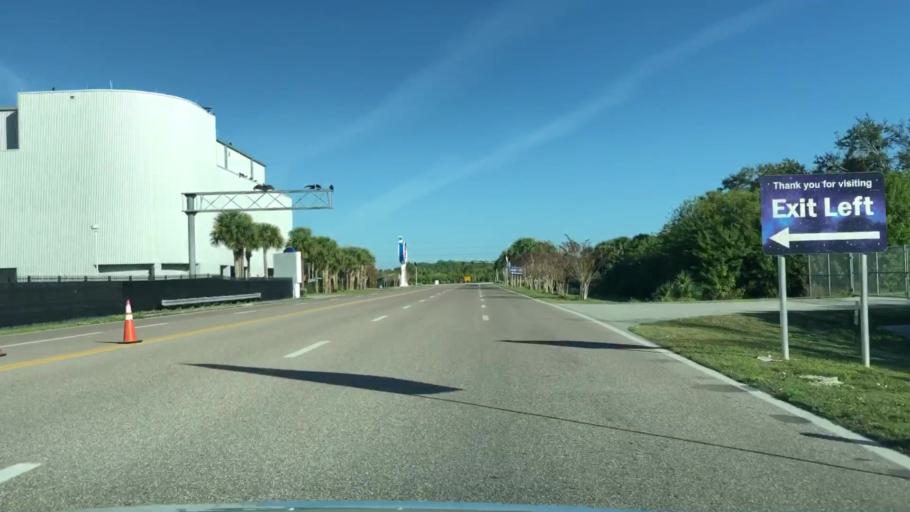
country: US
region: Florida
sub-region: Brevard County
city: Merritt Island
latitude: 28.5238
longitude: -80.6791
